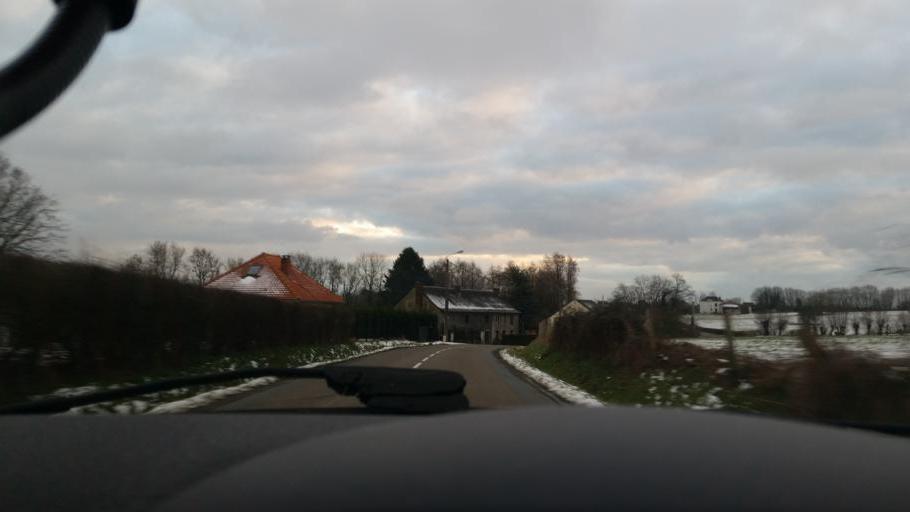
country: FR
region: Nord-Pas-de-Calais
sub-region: Departement du Nord
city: Marpent
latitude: 50.2461
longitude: 4.0978
